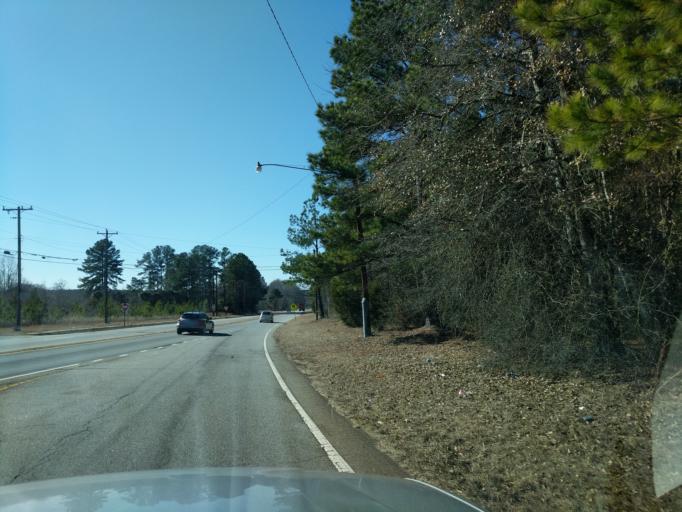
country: US
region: South Carolina
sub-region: Anderson County
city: Homeland Park
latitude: 34.4727
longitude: -82.6719
